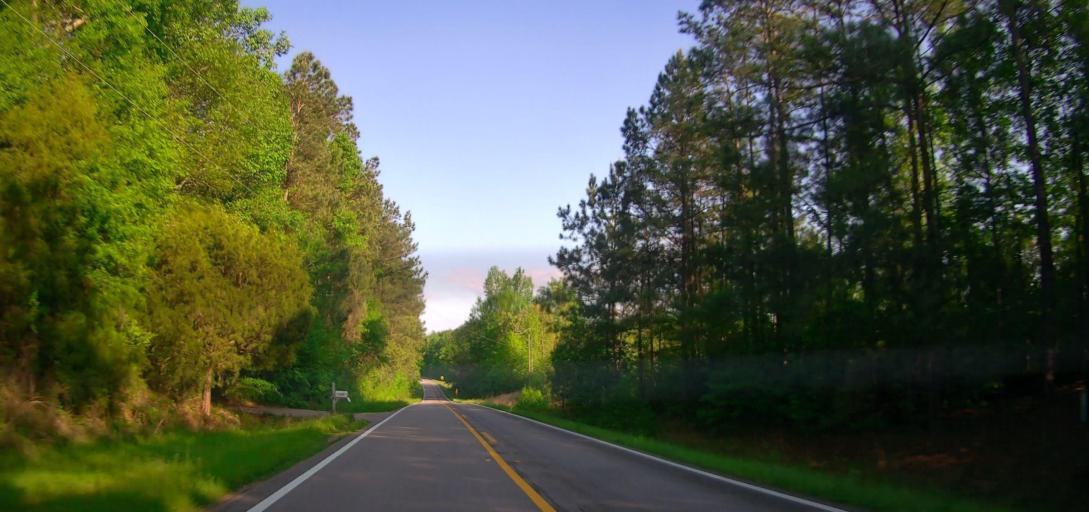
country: US
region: Georgia
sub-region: Putnam County
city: Eatonton
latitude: 33.3022
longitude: -83.3407
